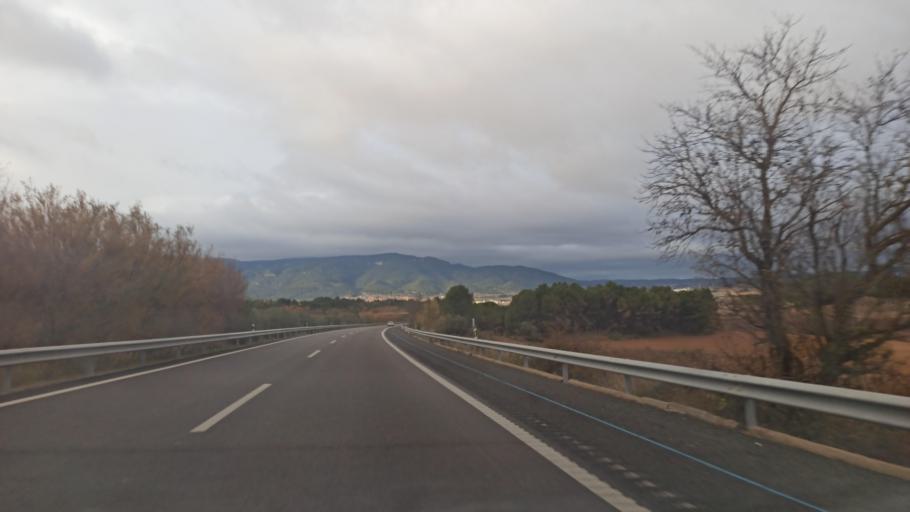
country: ES
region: Catalonia
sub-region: Provincia de Tarragona
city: Montblanc
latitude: 41.3893
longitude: 1.2116
